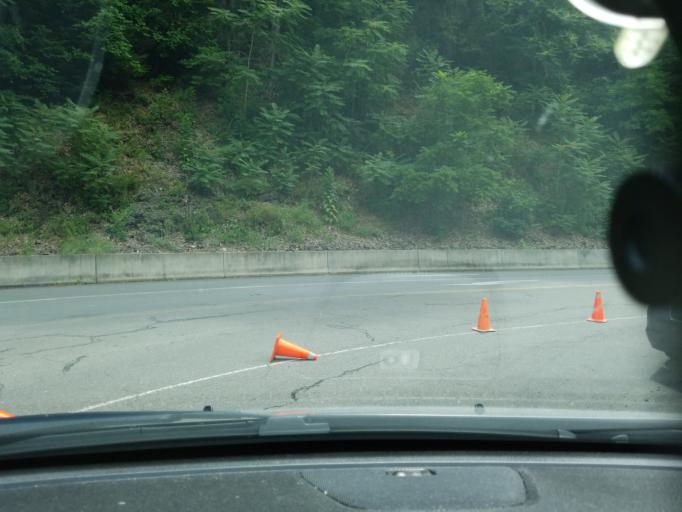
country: US
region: Pennsylvania
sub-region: Northumberland County
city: Elysburg
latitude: 40.8838
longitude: -76.5059
